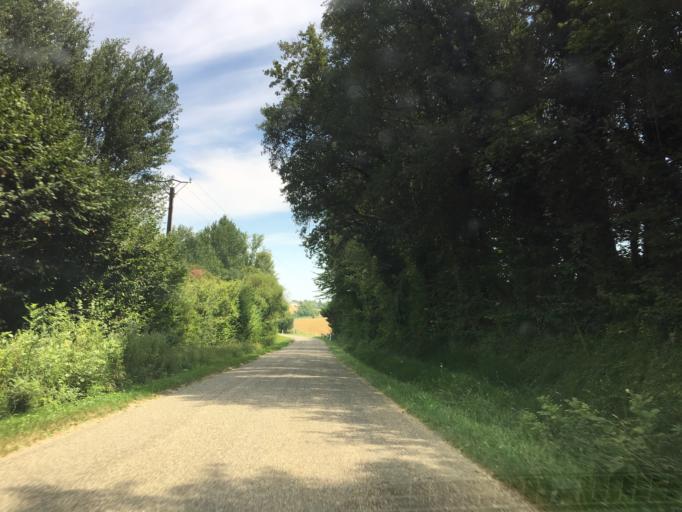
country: FR
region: Midi-Pyrenees
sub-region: Departement du Gers
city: Jegun
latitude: 43.8144
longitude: 0.5371
